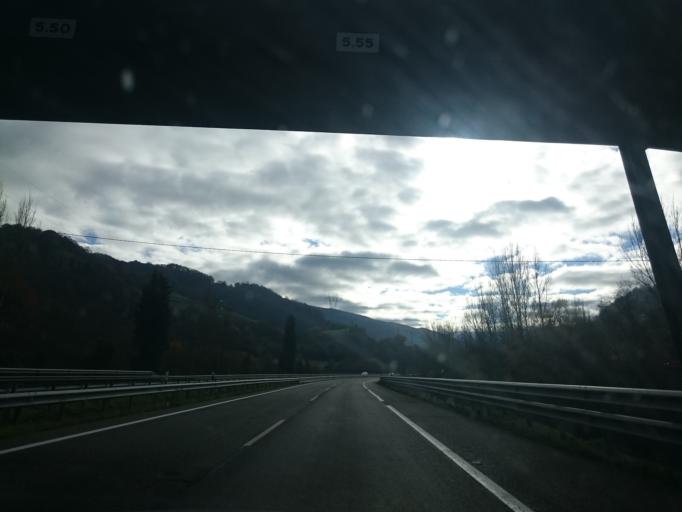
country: ES
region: Asturias
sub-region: Province of Asturias
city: Pola de Lena
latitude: 43.1267
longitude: -5.8159
